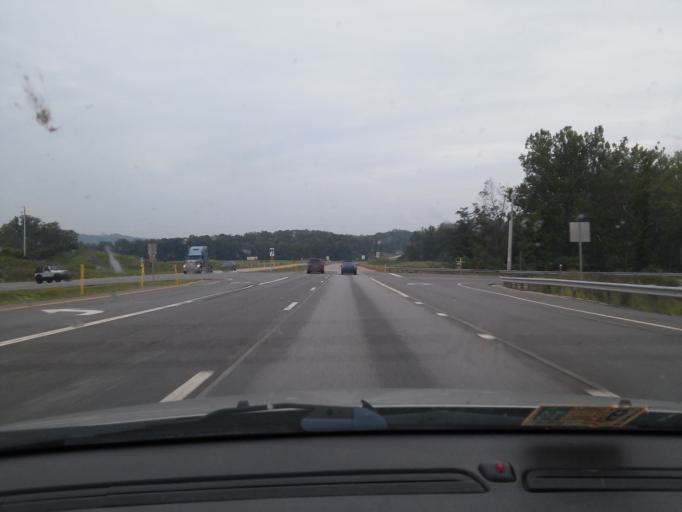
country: US
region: West Virginia
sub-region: Putnam County
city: Eleanor
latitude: 38.5488
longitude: -81.9808
